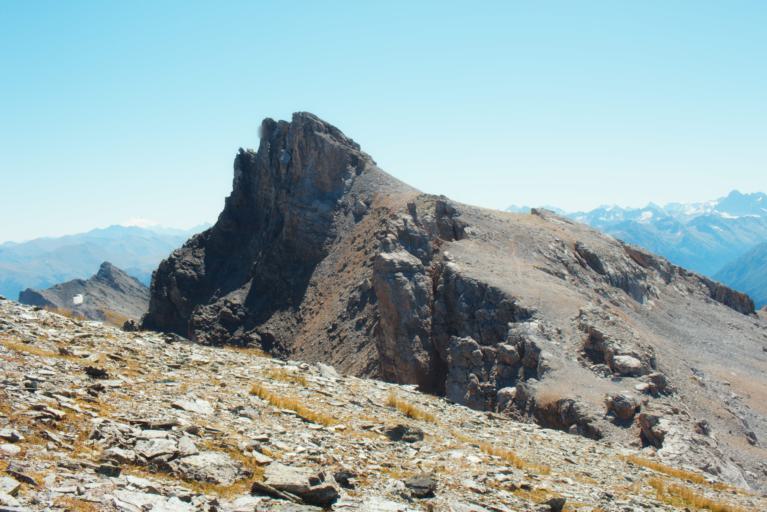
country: RU
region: Karachayevo-Cherkesiya
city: Nizhniy Arkhyz
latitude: 43.5853
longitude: 41.1950
